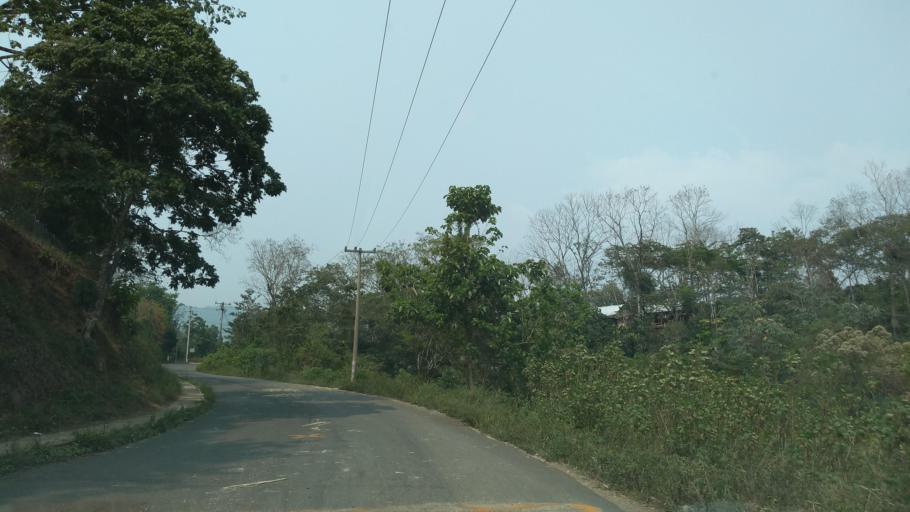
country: MX
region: Veracruz
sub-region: Tezonapa
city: Laguna Chica (Pueblo Nuevo)
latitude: 18.5425
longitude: -96.7714
